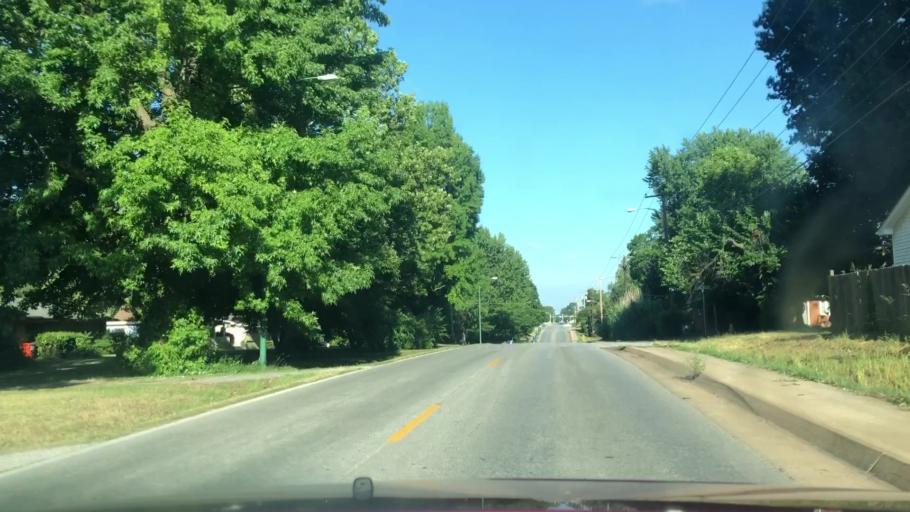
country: US
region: Missouri
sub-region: Greene County
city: Springfield
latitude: 37.1740
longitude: -93.2553
